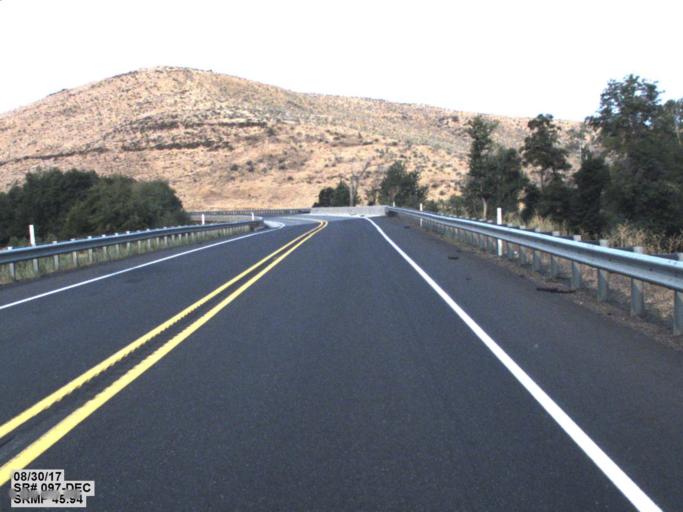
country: US
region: Washington
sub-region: Yakima County
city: Toppenish
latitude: 46.2042
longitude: -120.4765
